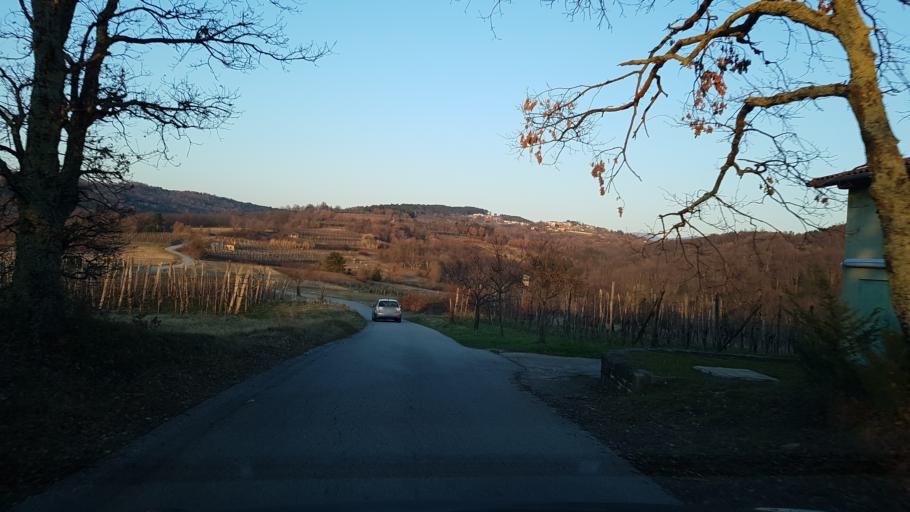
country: SI
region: Koper-Capodistria
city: Sv. Anton
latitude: 45.4887
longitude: 13.8409
